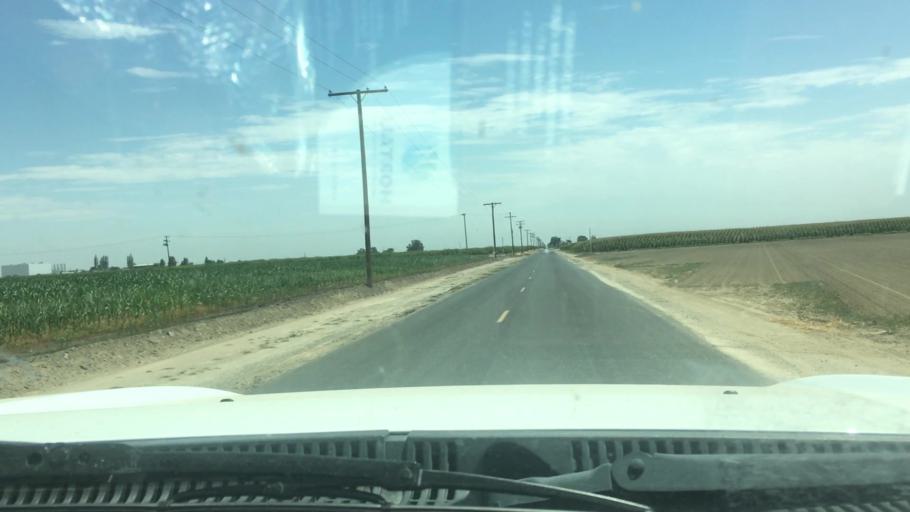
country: US
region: California
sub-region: Tulare County
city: Tipton
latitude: 36.0604
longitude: -119.3220
